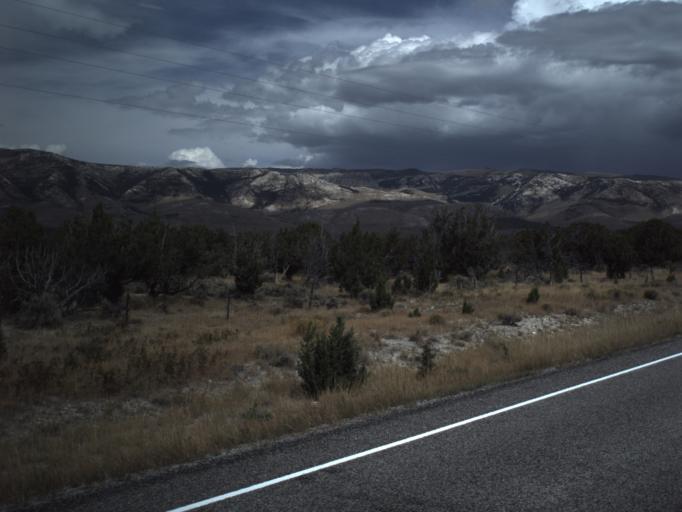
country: US
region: Idaho
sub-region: Cassia County
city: Burley
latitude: 41.8012
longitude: -113.4566
